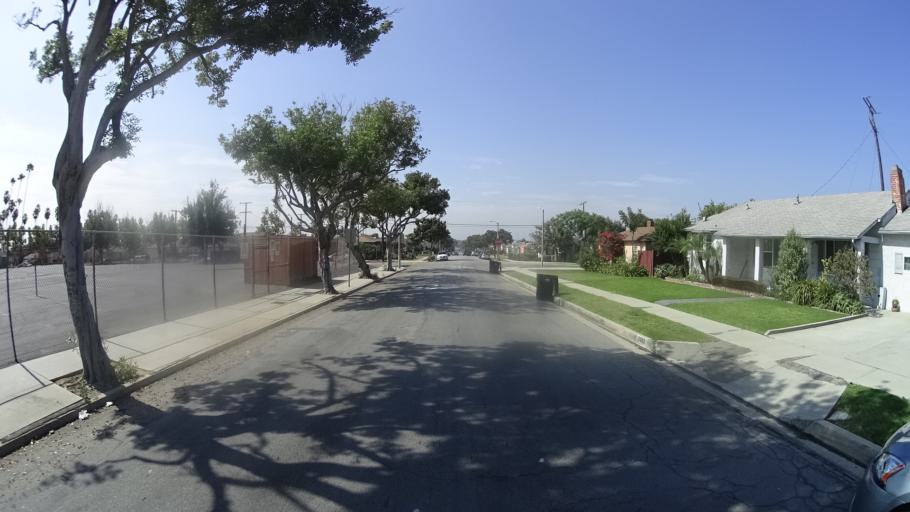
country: US
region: California
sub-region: Los Angeles County
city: View Park-Windsor Hills
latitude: 33.9914
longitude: -118.3438
